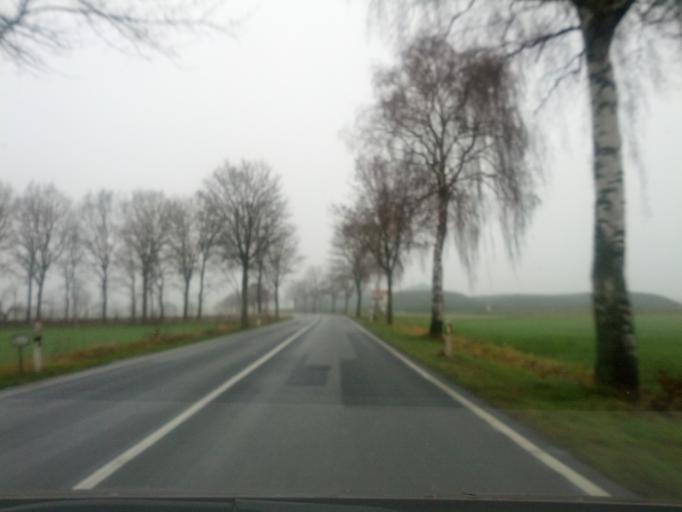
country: DE
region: Lower Saxony
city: Nottensdorf
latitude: 53.4565
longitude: 9.6024
